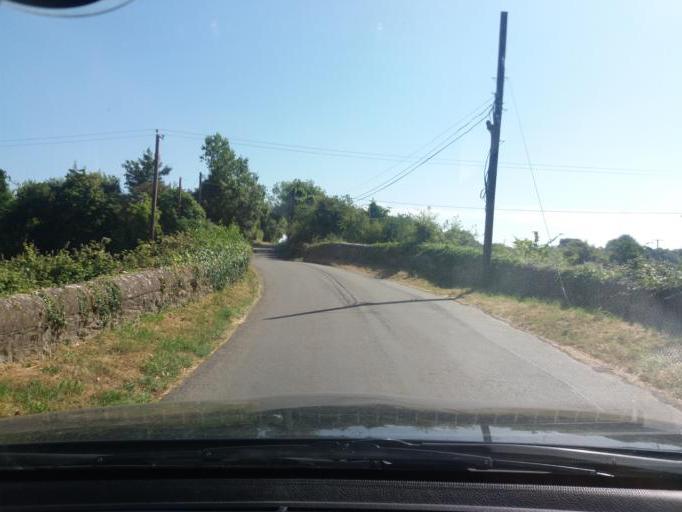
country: IE
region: Leinster
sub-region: Fingal County
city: Swords
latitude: 53.4892
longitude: -6.2851
